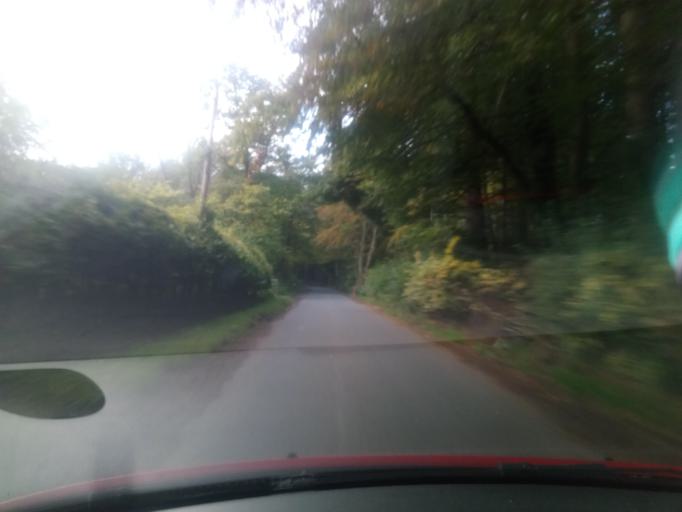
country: GB
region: Scotland
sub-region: The Scottish Borders
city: Jedburgh
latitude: 55.3785
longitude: -2.6470
